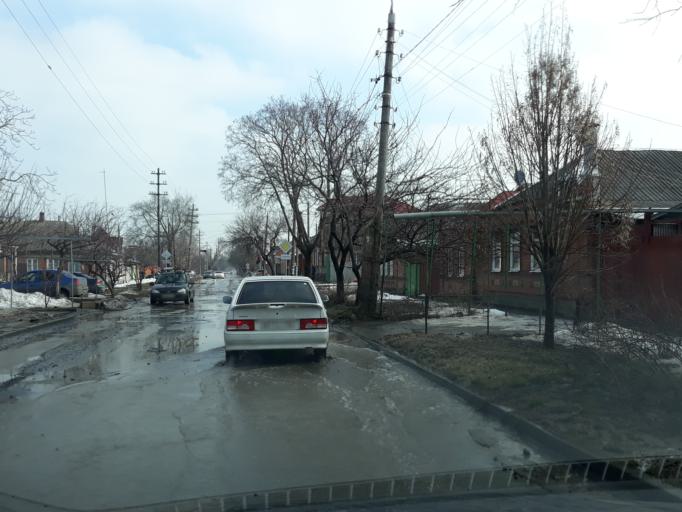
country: RU
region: Rostov
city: Taganrog
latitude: 47.2156
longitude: 38.8987
